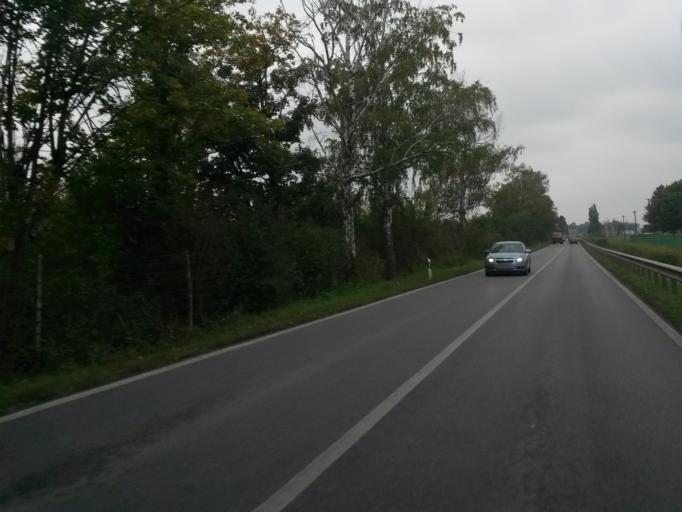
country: HR
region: Osjecko-Baranjska
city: Brijest
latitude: 45.5348
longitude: 18.6621
